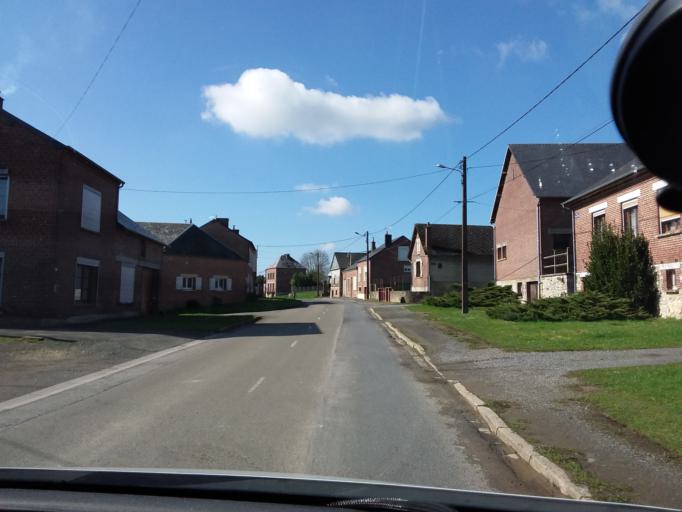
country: FR
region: Picardie
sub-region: Departement de l'Aisne
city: Origny-en-Thierache
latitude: 49.8083
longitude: 4.0166
